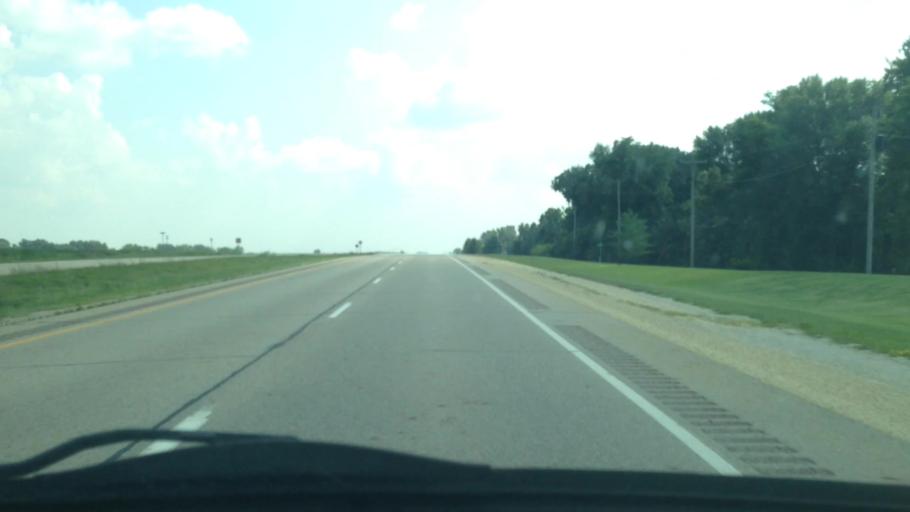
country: US
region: Iowa
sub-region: Bremer County
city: Denver
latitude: 42.5922
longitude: -92.3375
